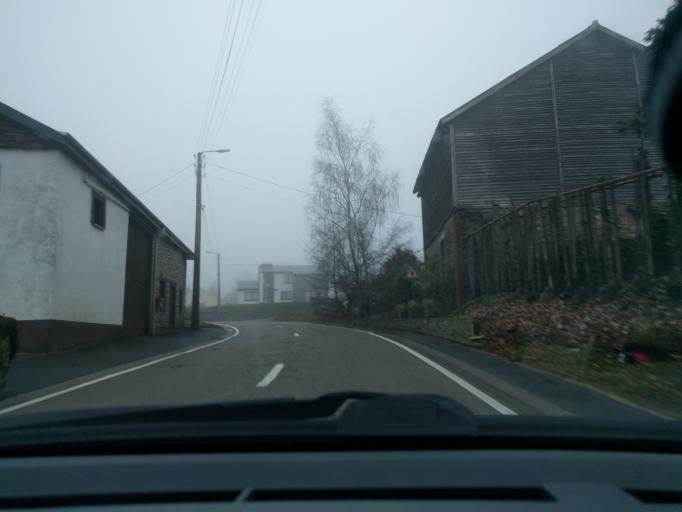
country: BE
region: Wallonia
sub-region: Province du Luxembourg
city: Gouvy
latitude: 50.1947
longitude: 5.9239
